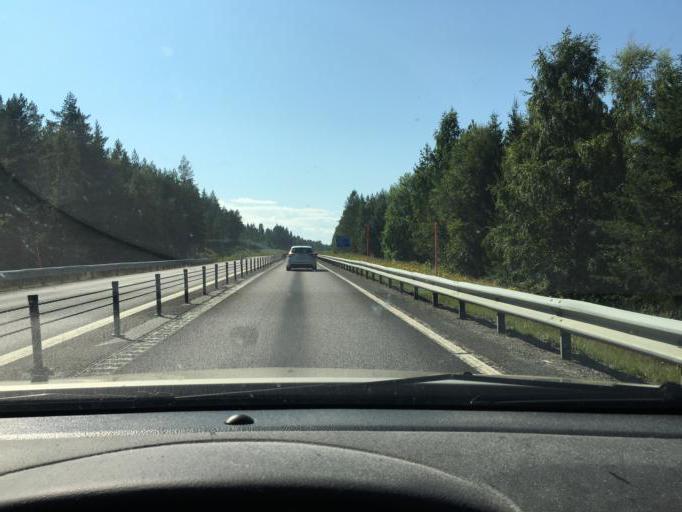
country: SE
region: Norrbotten
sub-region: Lulea Kommun
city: Gammelstad
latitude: 65.5873
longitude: 22.0159
